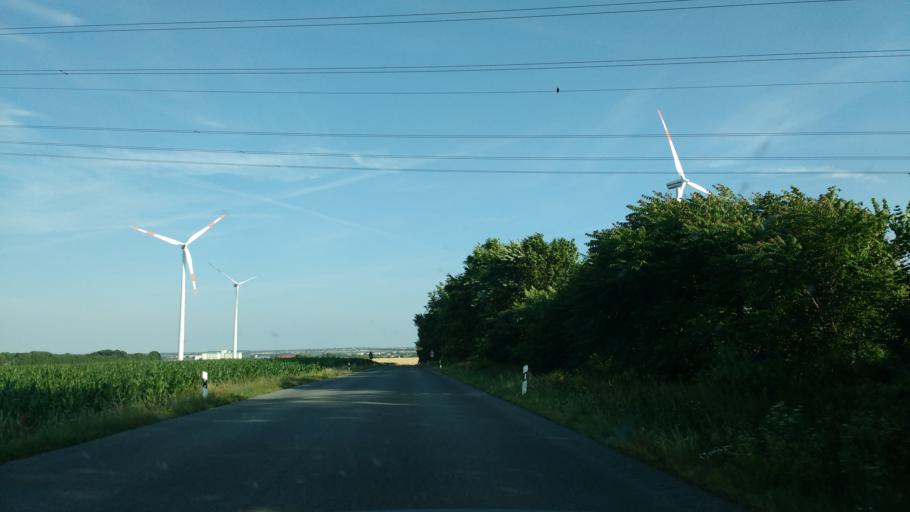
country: DE
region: Saxony-Anhalt
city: Farnstadt
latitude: 51.4149
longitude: 11.5759
